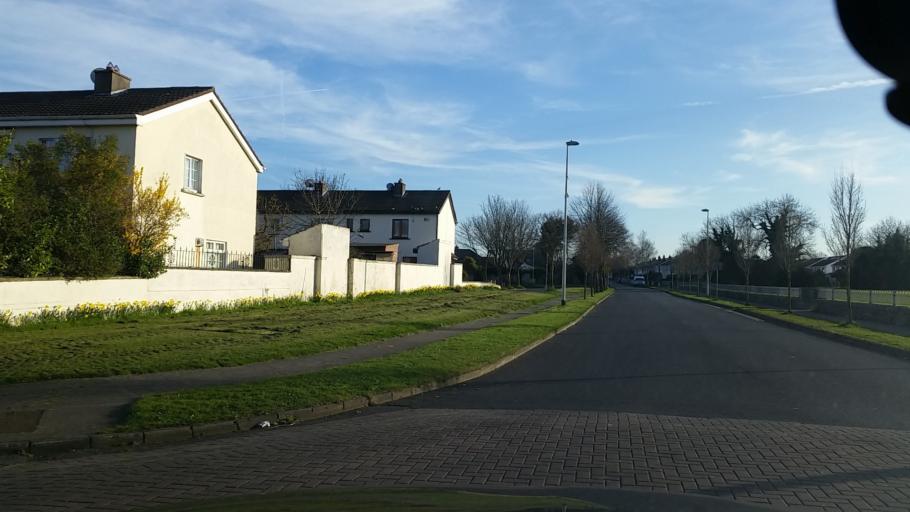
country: IE
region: Leinster
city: Hartstown
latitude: 53.3898
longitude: -6.4047
